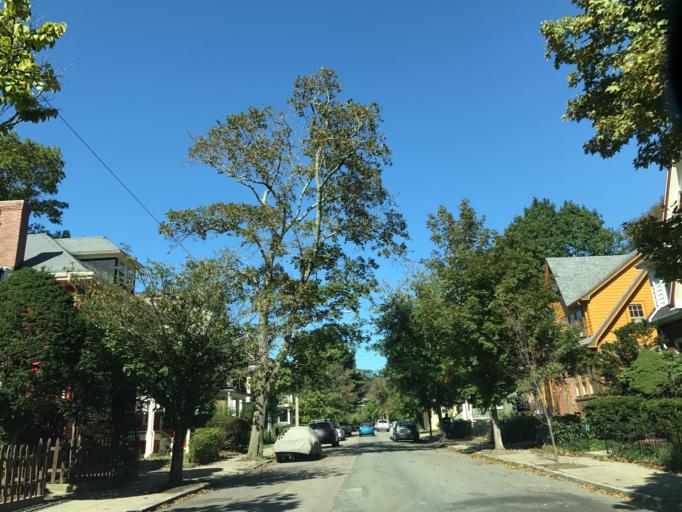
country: US
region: Massachusetts
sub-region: Suffolk County
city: Jamaica Plain
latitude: 42.3114
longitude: -71.1190
